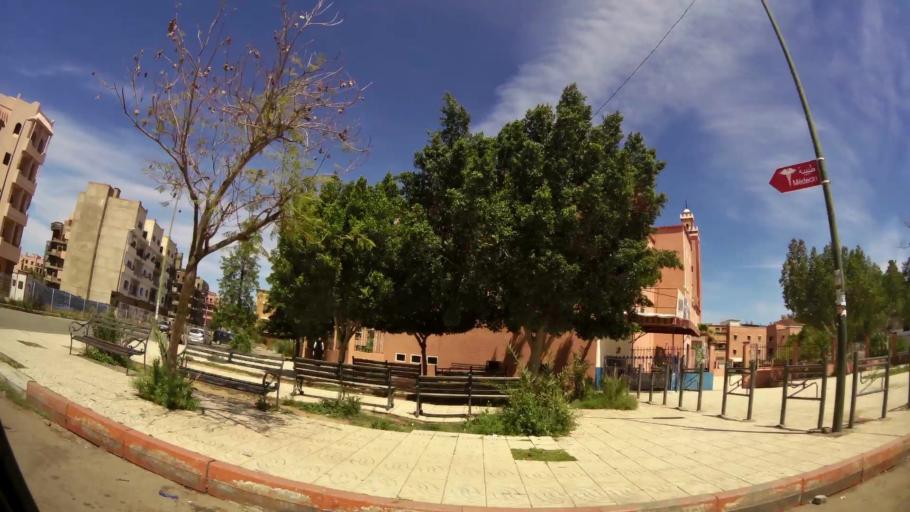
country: MA
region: Marrakech-Tensift-Al Haouz
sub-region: Marrakech
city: Marrakesh
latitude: 31.6593
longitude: -7.9896
